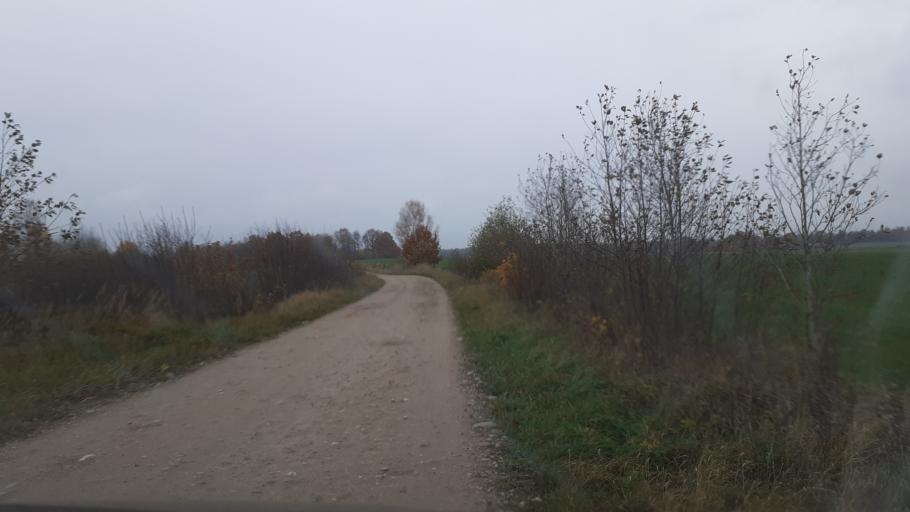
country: LV
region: Saldus Rajons
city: Saldus
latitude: 56.8670
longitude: 22.3435
